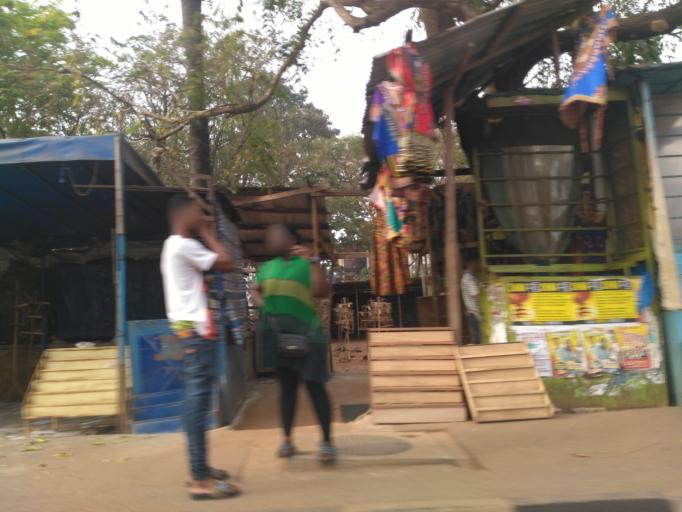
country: GH
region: Ashanti
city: Kumasi
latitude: 6.6911
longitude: -1.6243
